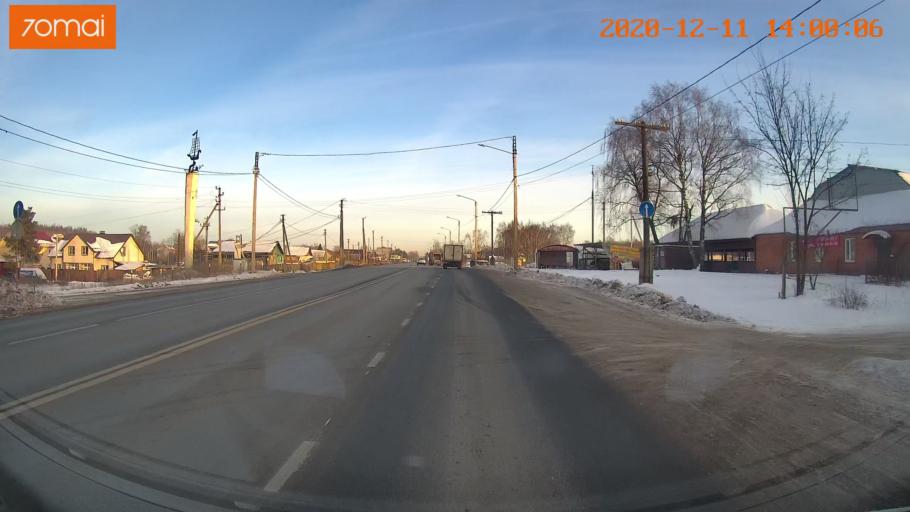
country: RU
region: Kostroma
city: Oktyabr'skiy
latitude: 57.7837
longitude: 41.0233
